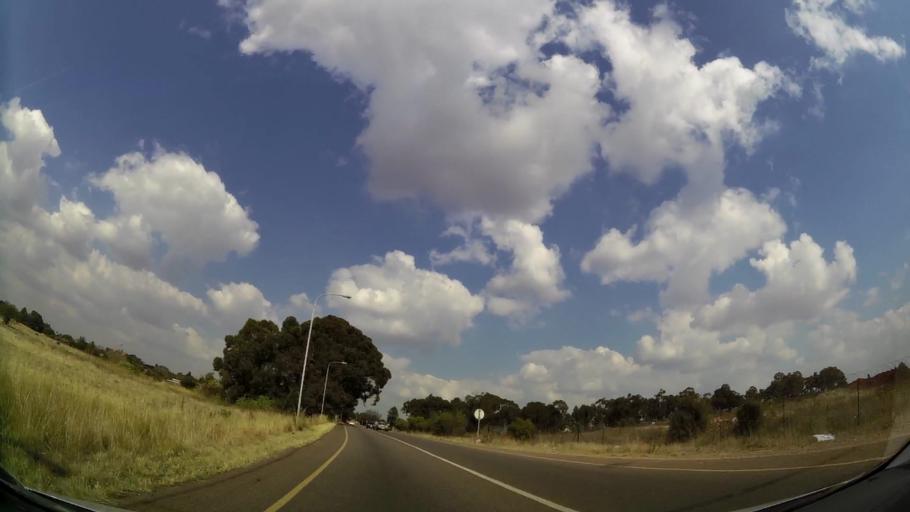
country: ZA
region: Gauteng
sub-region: City of Tshwane Metropolitan Municipality
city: Centurion
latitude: -25.8228
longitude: 28.2363
